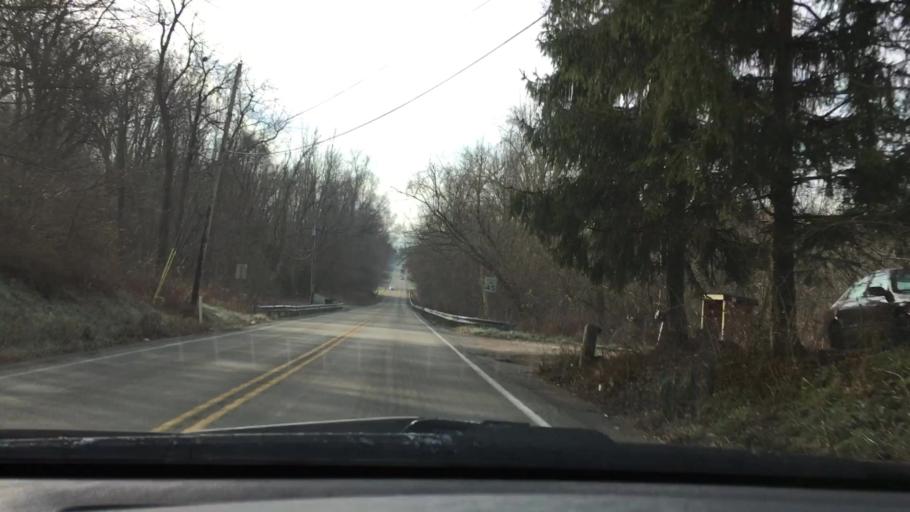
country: US
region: Pennsylvania
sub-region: Allegheny County
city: Industry
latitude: 40.2651
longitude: -79.7678
